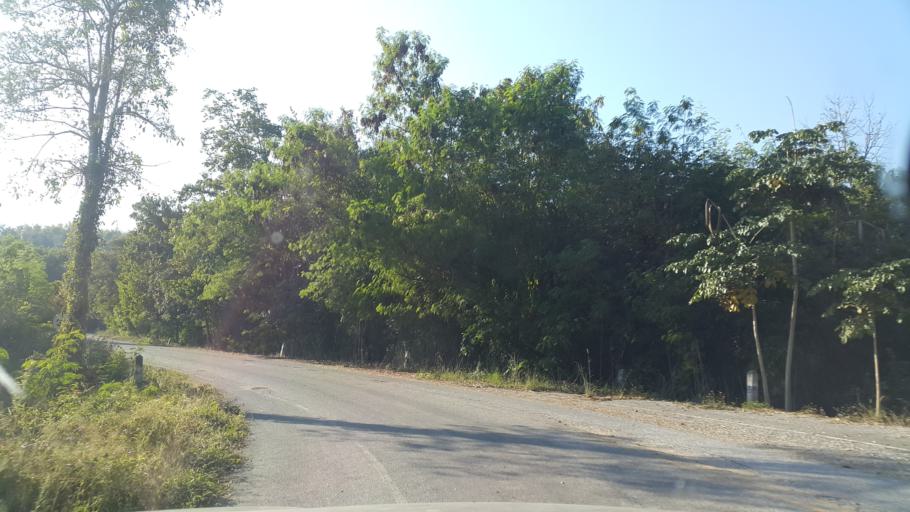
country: TH
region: Sukhothai
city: Thung Saliam
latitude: 17.3864
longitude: 99.5204
